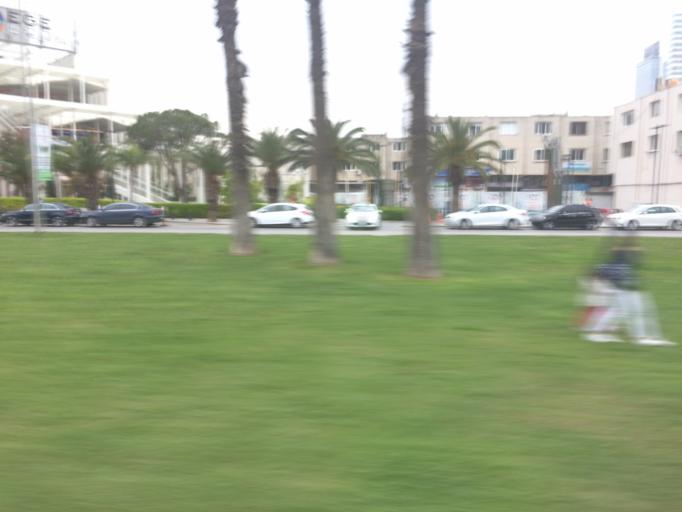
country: TR
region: Izmir
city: Buca
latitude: 38.4467
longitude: 27.1766
